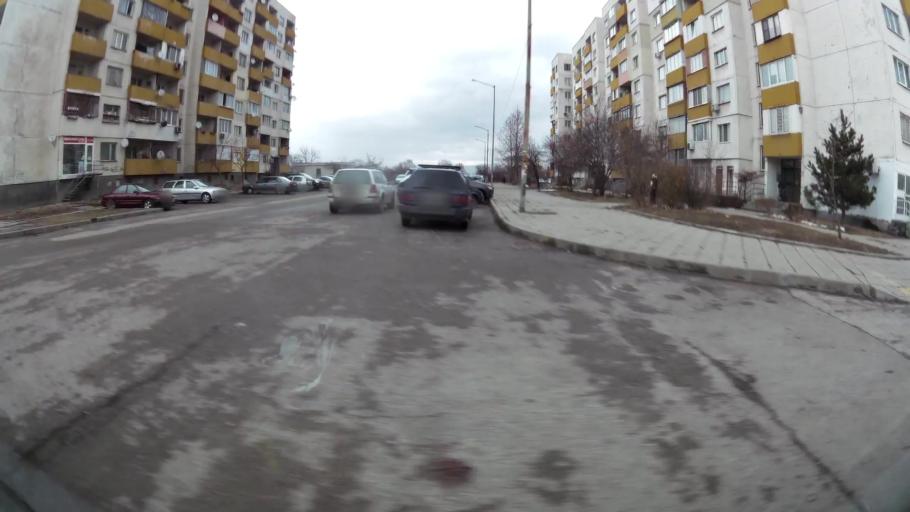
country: BG
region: Sofia-Capital
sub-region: Stolichna Obshtina
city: Sofia
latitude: 42.7227
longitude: 23.2756
